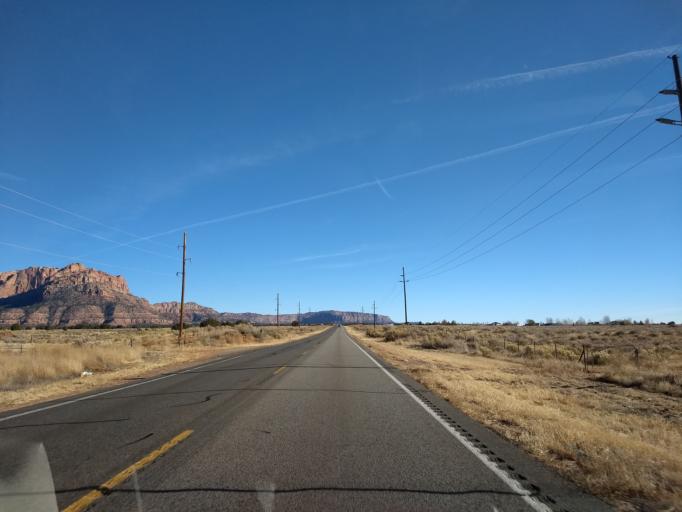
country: US
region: Arizona
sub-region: Mohave County
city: Colorado City
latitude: 37.0322
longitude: -113.0598
